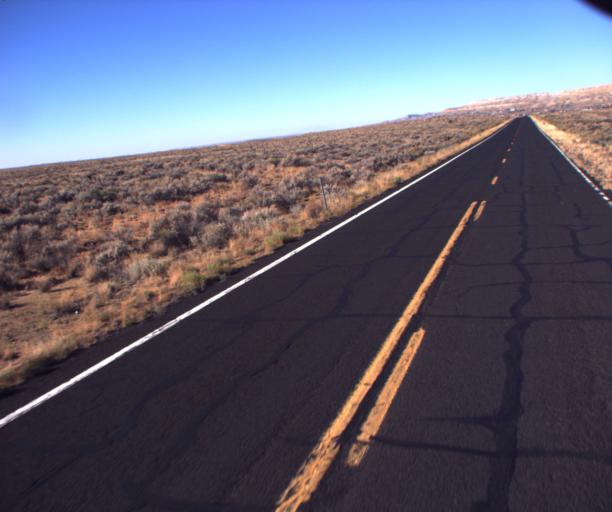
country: US
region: Arizona
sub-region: Navajo County
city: First Mesa
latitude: 35.8419
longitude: -110.3283
